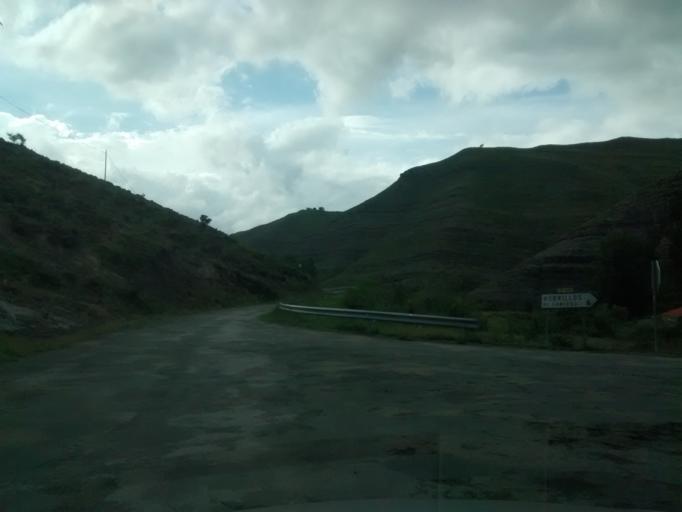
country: ES
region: La Rioja
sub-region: Provincia de La Rioja
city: San Roman de Cameros
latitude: 42.2182
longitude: -2.4668
